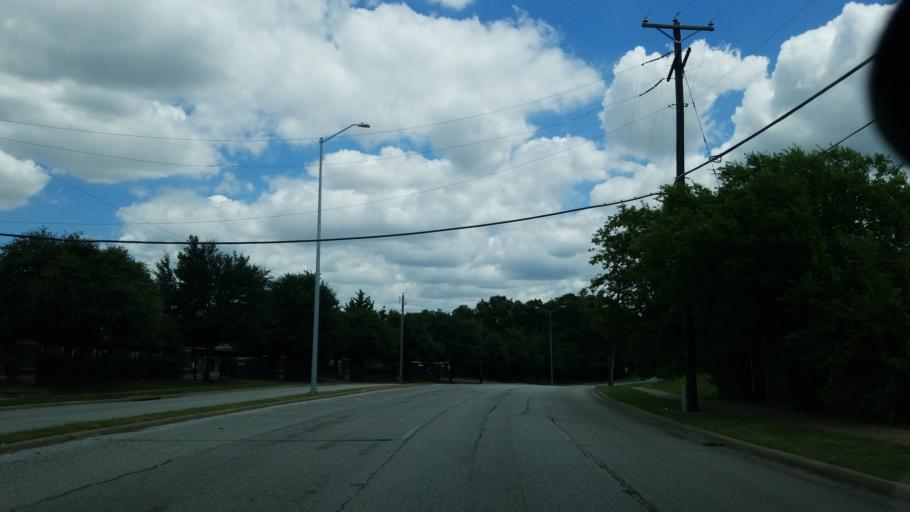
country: US
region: Texas
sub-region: Dallas County
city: Dallas
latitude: 32.7182
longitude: -96.7738
